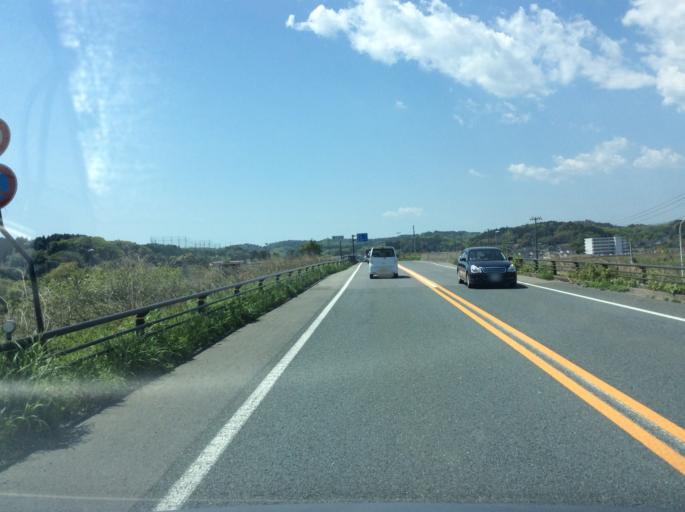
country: JP
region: Ibaraki
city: Kitaibaraki
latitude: 36.8950
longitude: 140.7882
